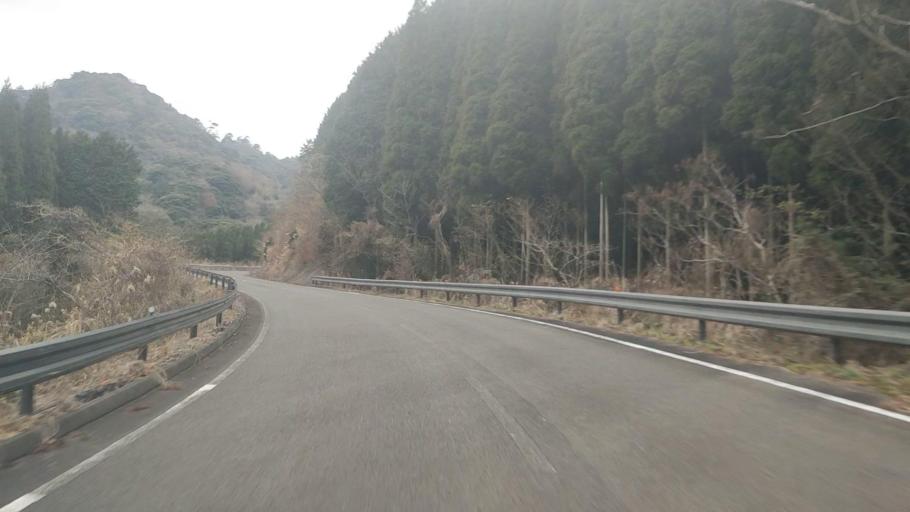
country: JP
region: Nagasaki
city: Shimabara
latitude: 32.7850
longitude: 130.2820
